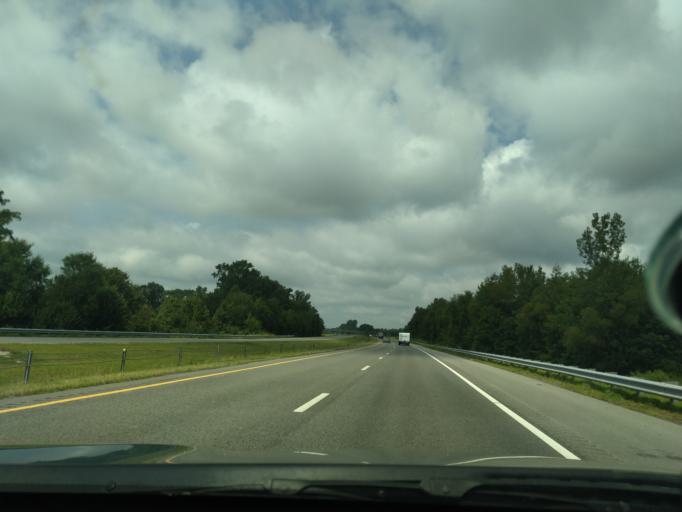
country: US
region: North Carolina
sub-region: Martin County
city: Robersonville
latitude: 35.8334
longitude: -77.3089
